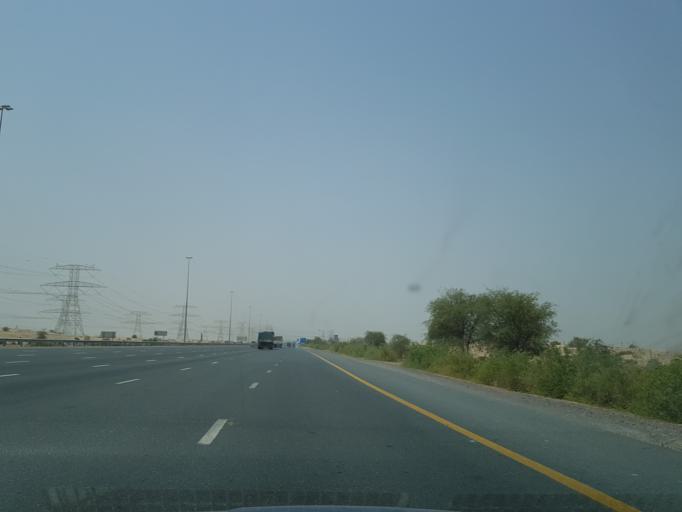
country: AE
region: Dubai
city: Dubai
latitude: 25.0470
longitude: 55.3061
